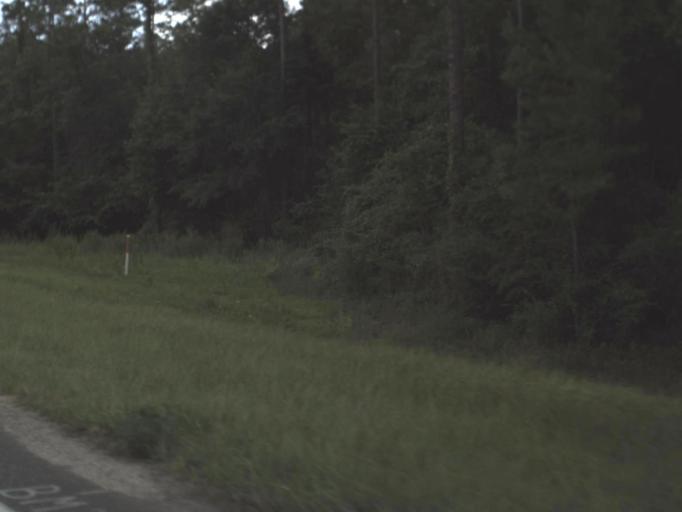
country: US
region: Florida
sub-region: Madison County
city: Madison
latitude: 30.3924
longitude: -83.1983
